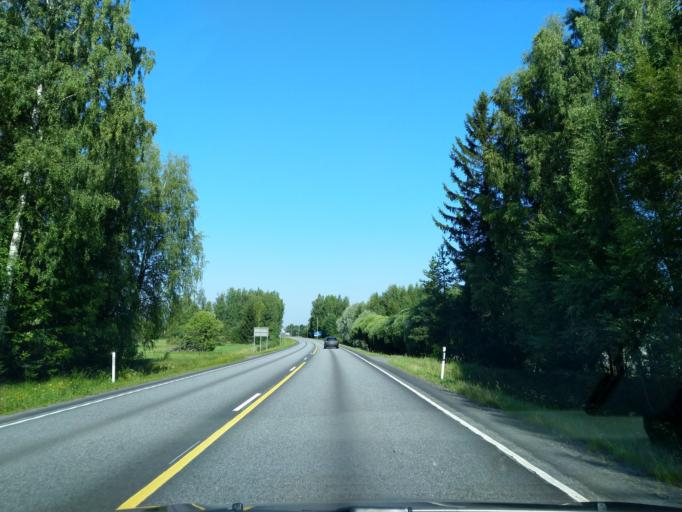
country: FI
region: Satakunta
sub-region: Pori
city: Huittinen
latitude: 61.1636
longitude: 22.7154
